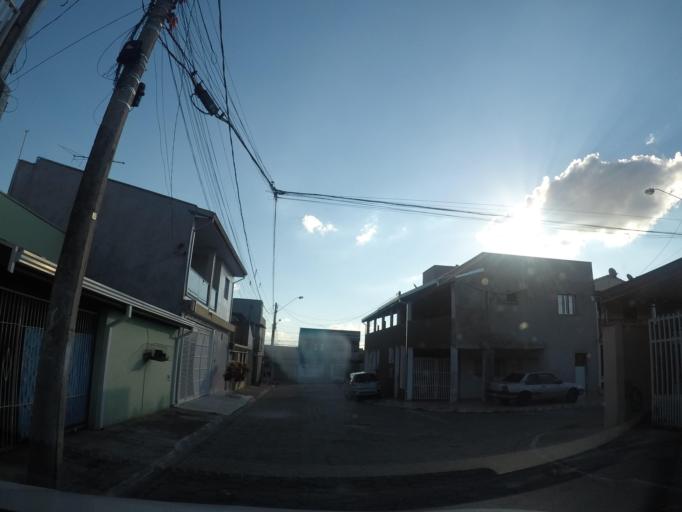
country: BR
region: Sao Paulo
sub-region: Sumare
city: Sumare
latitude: -22.8133
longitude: -47.2267
